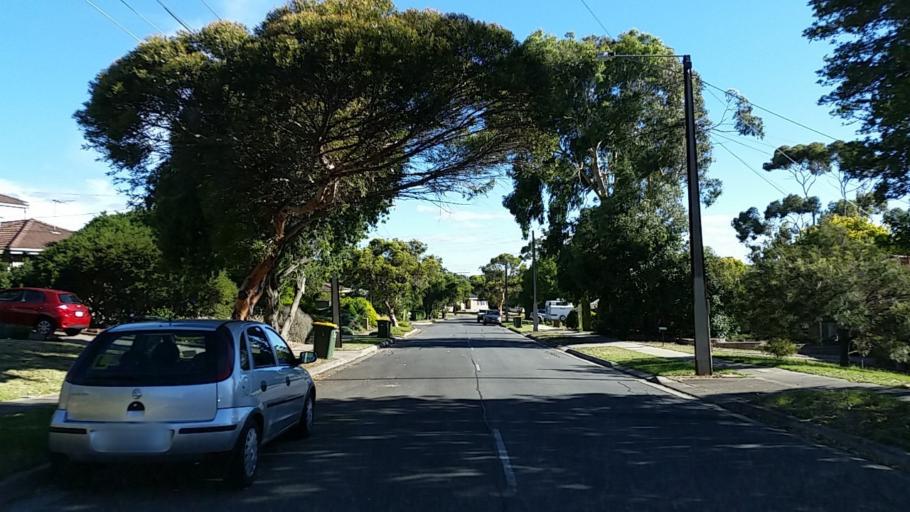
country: AU
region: South Australia
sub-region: Tea Tree Gully
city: Modbury
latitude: -34.8192
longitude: 138.6886
